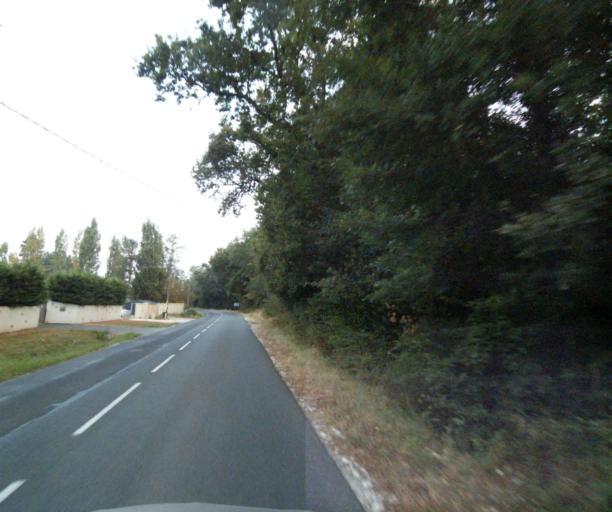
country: FR
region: Aquitaine
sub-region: Departement de la Gironde
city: La Sauve
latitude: 44.7603
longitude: -0.3298
